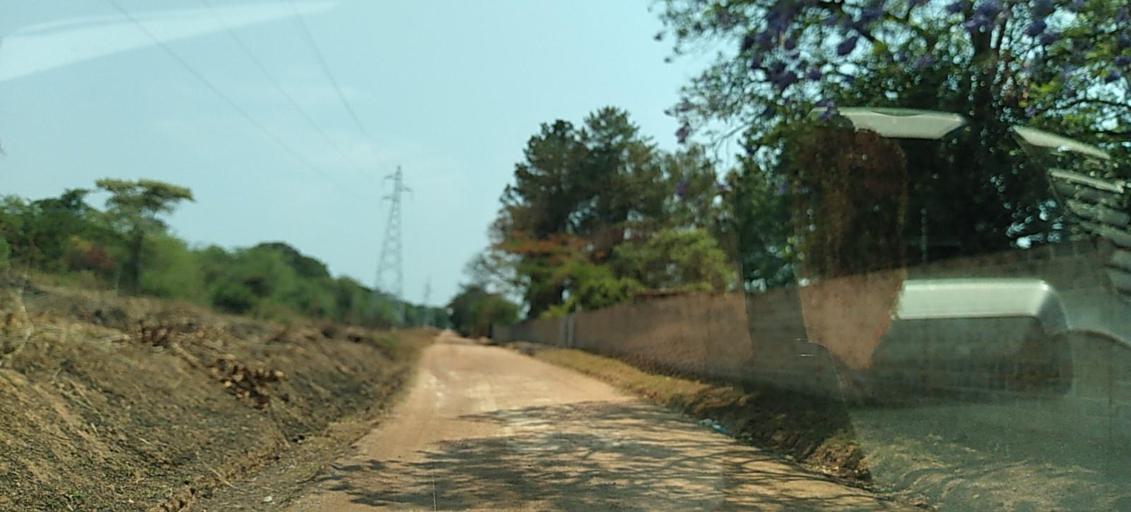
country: ZM
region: Copperbelt
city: Chambishi
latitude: -12.6156
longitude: 27.9504
